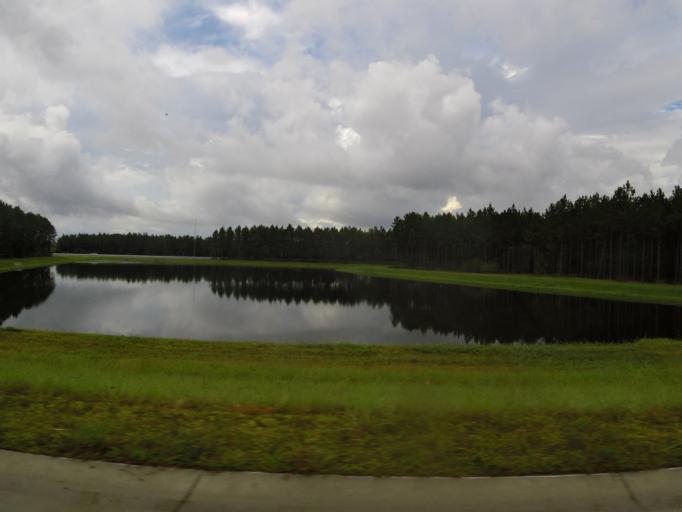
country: US
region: Florida
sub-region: Duval County
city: Baldwin
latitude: 30.3036
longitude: -81.8771
